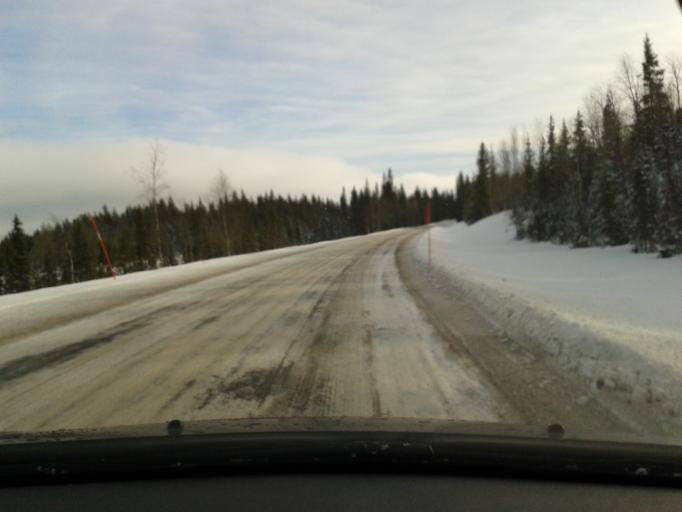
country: SE
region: Vaesterbotten
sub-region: Vilhelmina Kommun
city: Sjoberg
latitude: 64.7442
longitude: 16.1936
